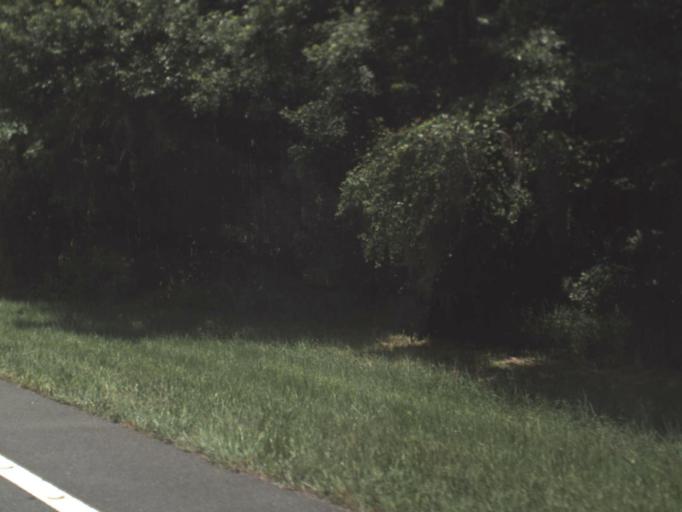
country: US
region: Florida
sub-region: Alachua County
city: Archer
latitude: 29.5030
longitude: -82.4065
